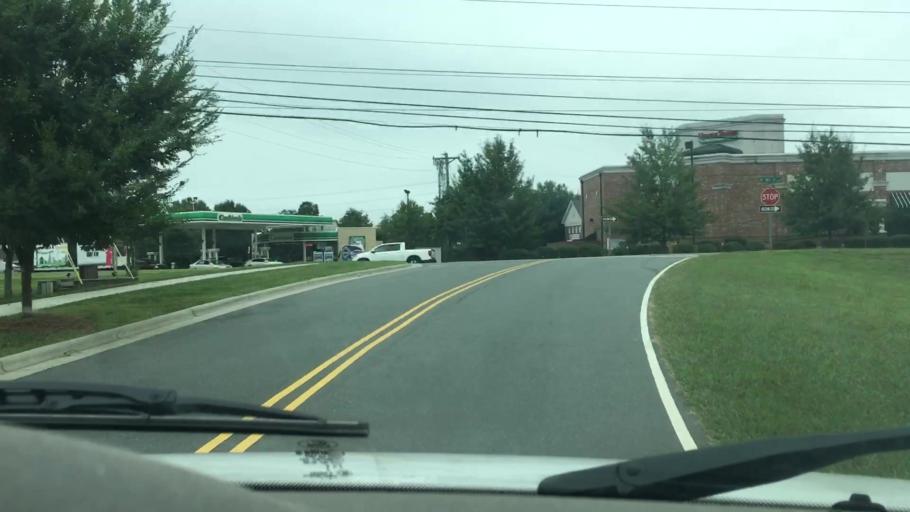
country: US
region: North Carolina
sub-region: Mecklenburg County
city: Cornelius
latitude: 35.4449
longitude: -80.8957
